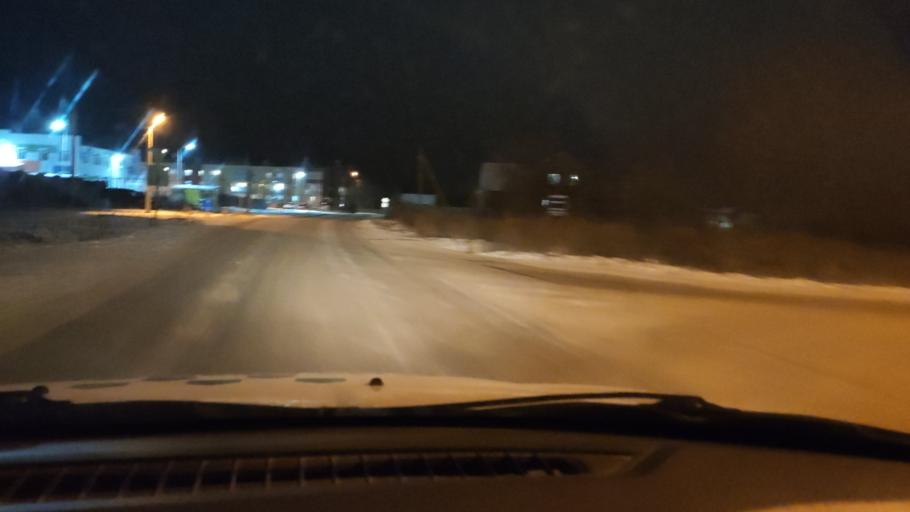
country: RU
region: Perm
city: Ferma
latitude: 57.8953
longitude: 56.3260
